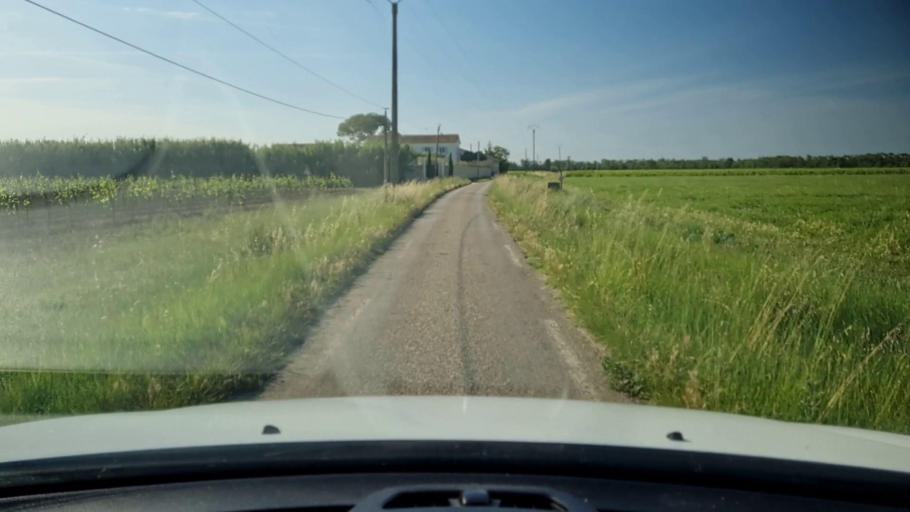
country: FR
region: Languedoc-Roussillon
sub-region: Departement du Gard
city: Le Cailar
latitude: 43.6402
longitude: 4.2299
